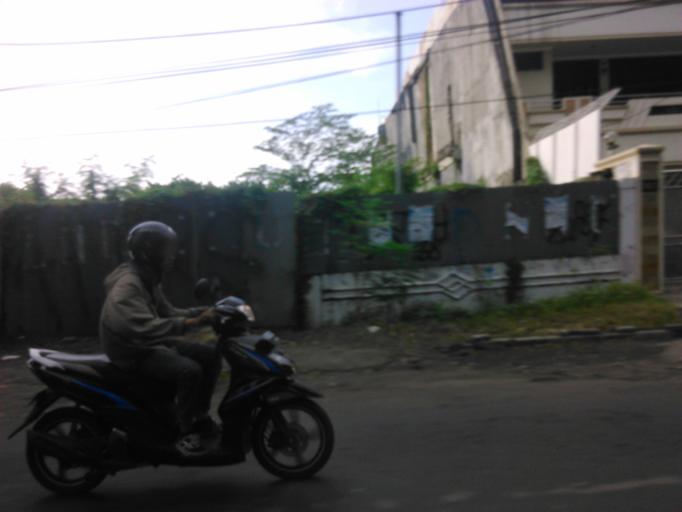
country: ID
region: East Java
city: Gubengairlangga
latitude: -7.2804
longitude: 112.7726
